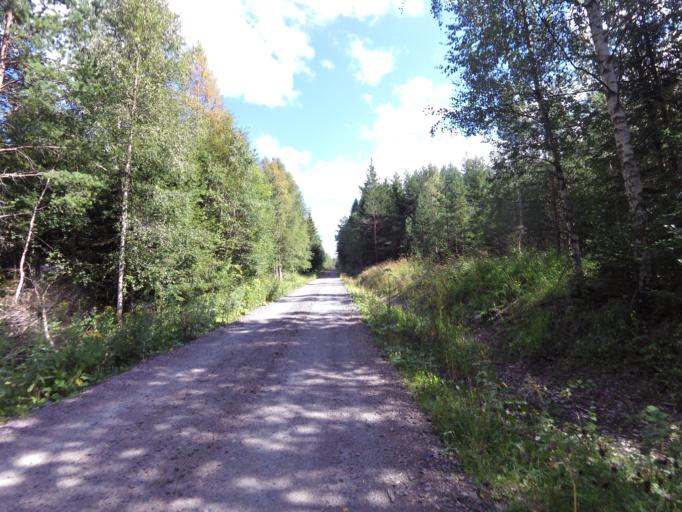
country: SE
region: Gaevleborg
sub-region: Hofors Kommun
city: Hofors
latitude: 60.5204
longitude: 16.2778
